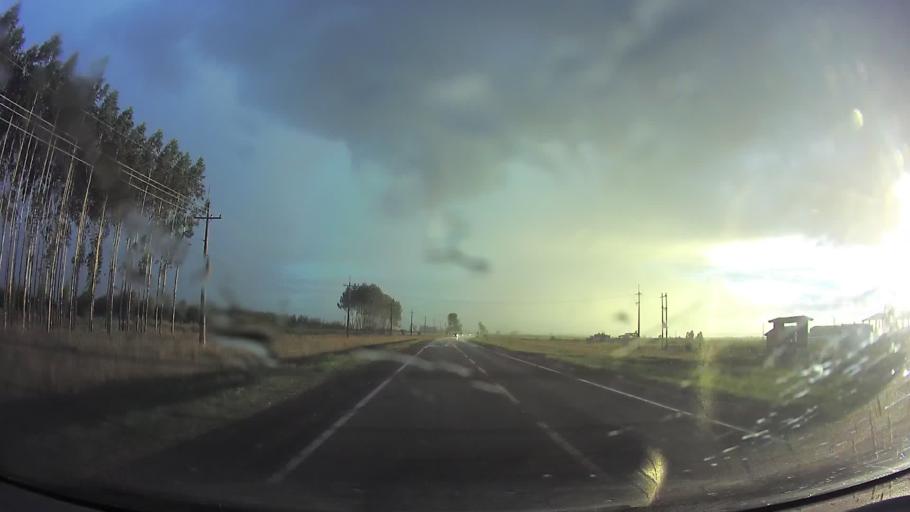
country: PY
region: Paraguari
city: Paraguari
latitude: -25.6757
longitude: -57.1664
